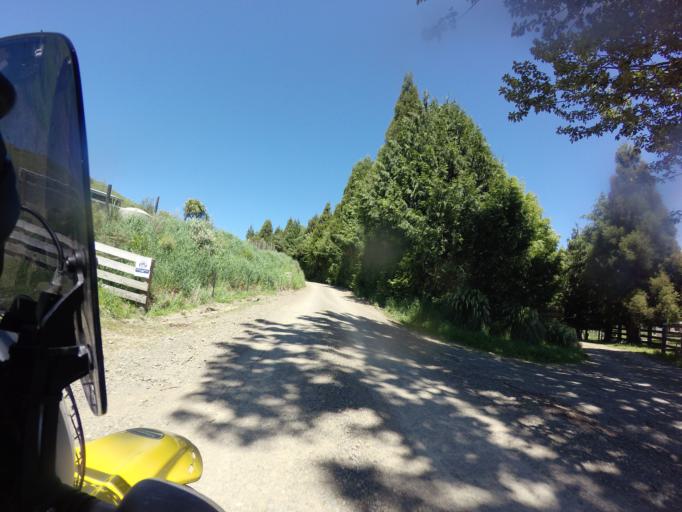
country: NZ
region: Bay of Plenty
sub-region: Opotiki District
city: Opotiki
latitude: -38.3976
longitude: 177.4585
